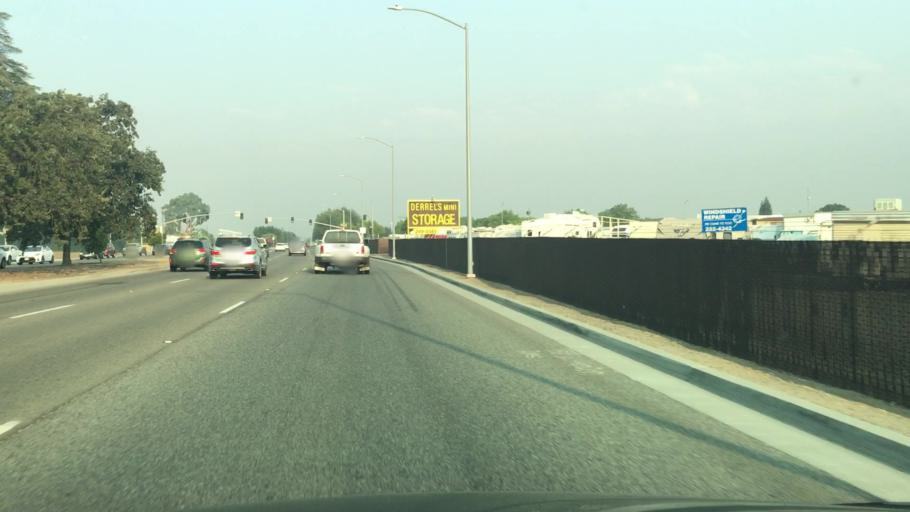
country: US
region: California
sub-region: Fresno County
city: Clovis
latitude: 36.8377
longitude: -119.7116
